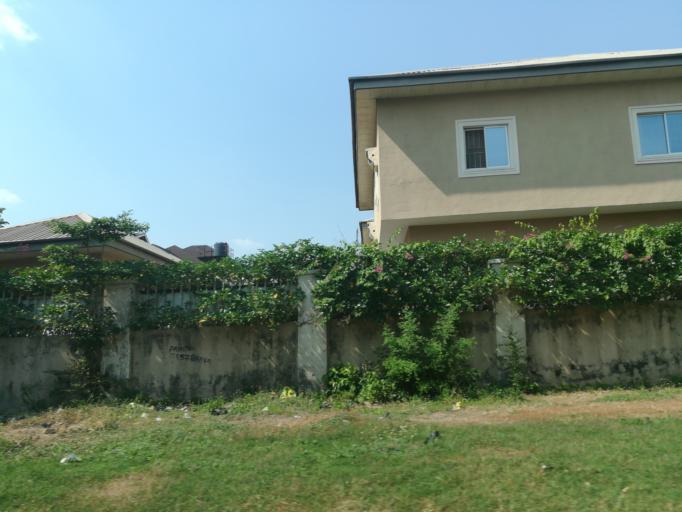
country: NG
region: Abuja Federal Capital Territory
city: Abuja
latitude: 9.0619
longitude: 7.4272
